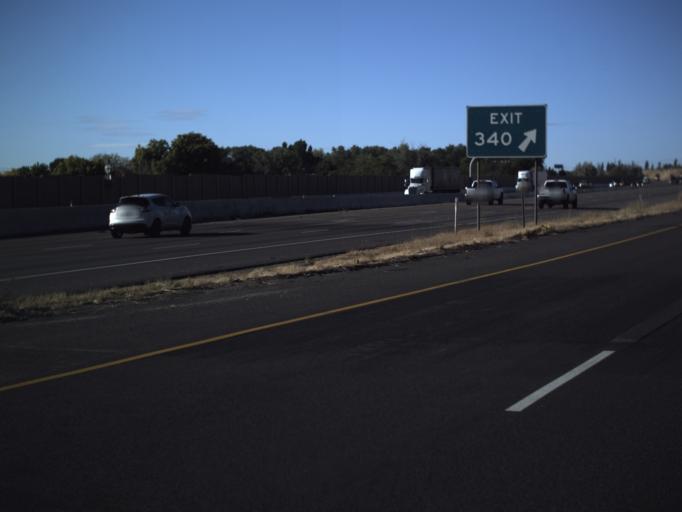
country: US
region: Utah
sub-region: Weber County
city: Riverdale
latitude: 41.1912
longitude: -112.0058
